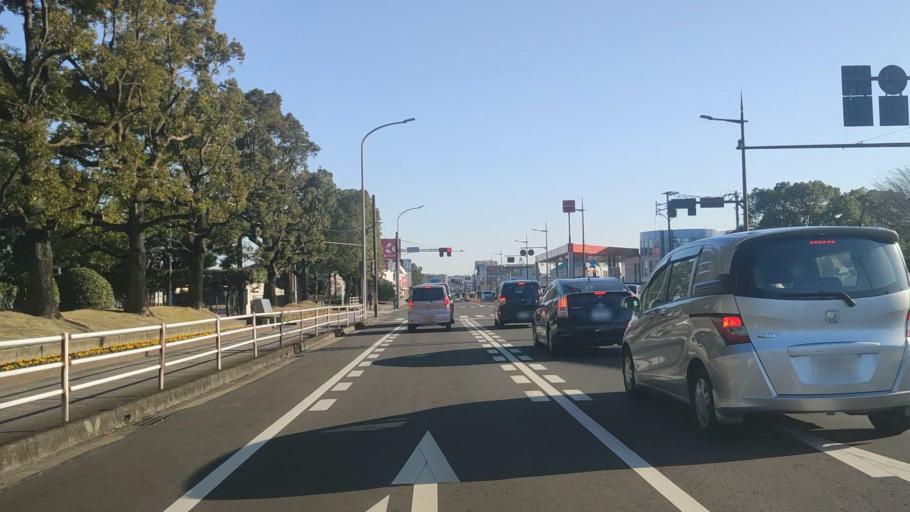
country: JP
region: Oita
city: Oita
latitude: 33.2087
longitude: 131.6002
